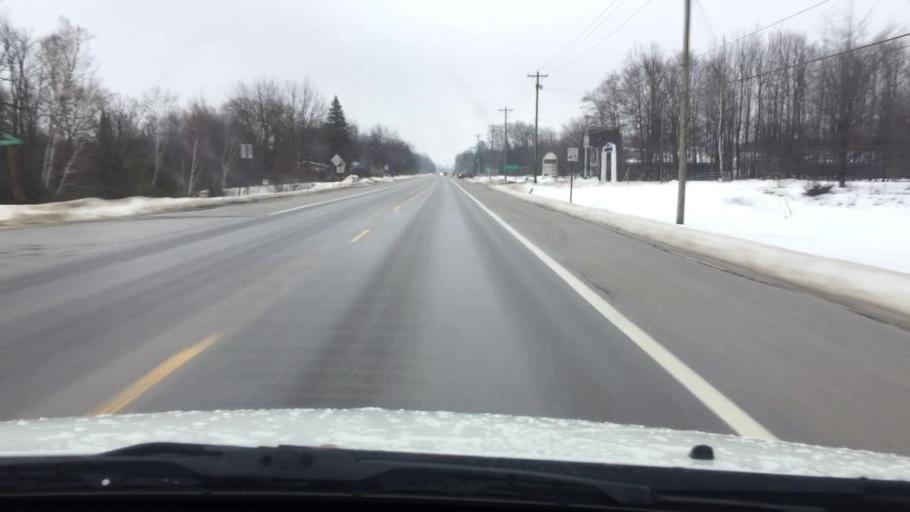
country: US
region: Michigan
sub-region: Charlevoix County
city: Charlevoix
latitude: 45.2942
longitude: -85.2520
